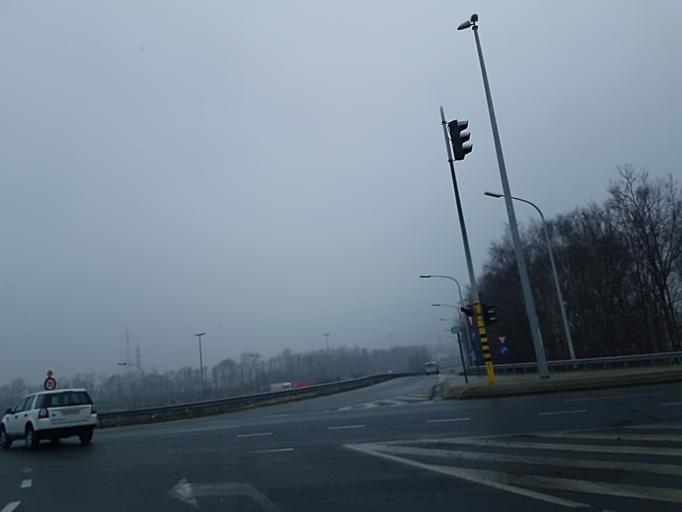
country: BE
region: Flanders
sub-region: Provincie Oost-Vlaanderen
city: Sint-Niklaas
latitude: 51.1366
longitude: 4.1435
